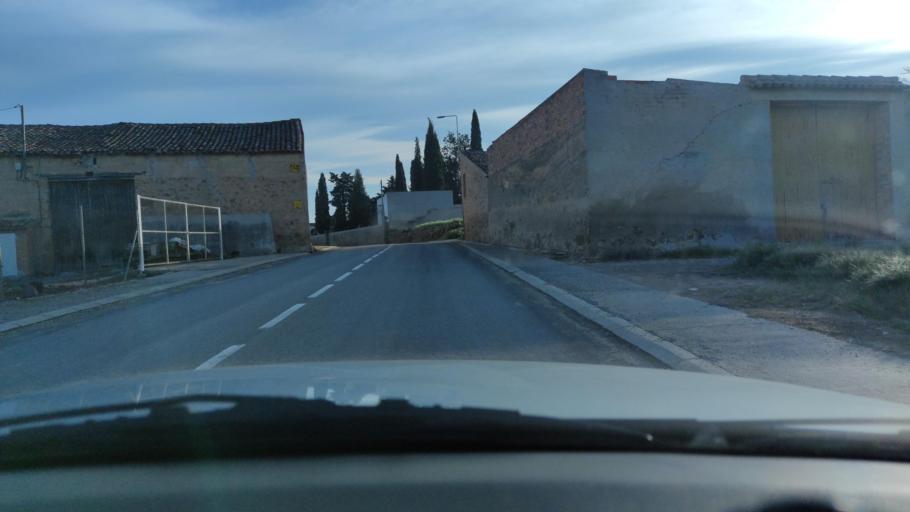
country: ES
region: Catalonia
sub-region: Provincia de Lleida
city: Agramunt
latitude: 41.7954
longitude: 1.0531
